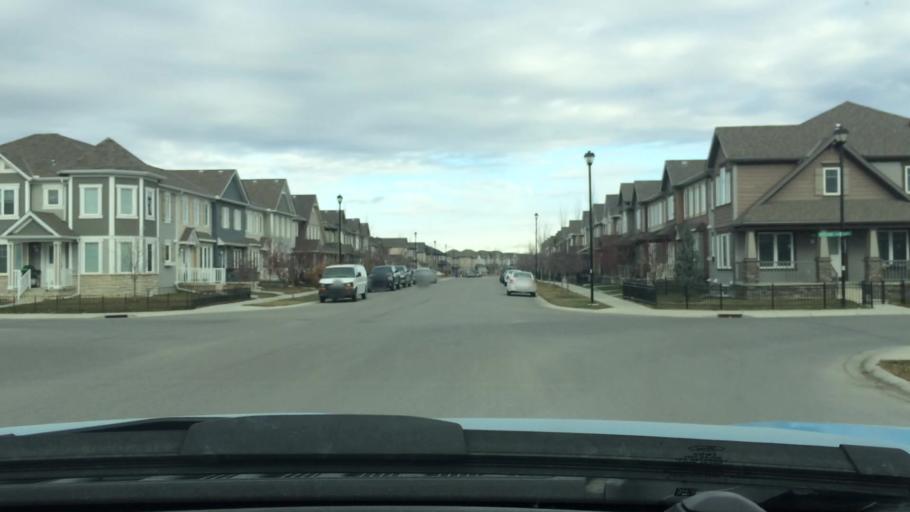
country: CA
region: Alberta
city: Airdrie
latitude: 51.2573
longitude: -114.0323
